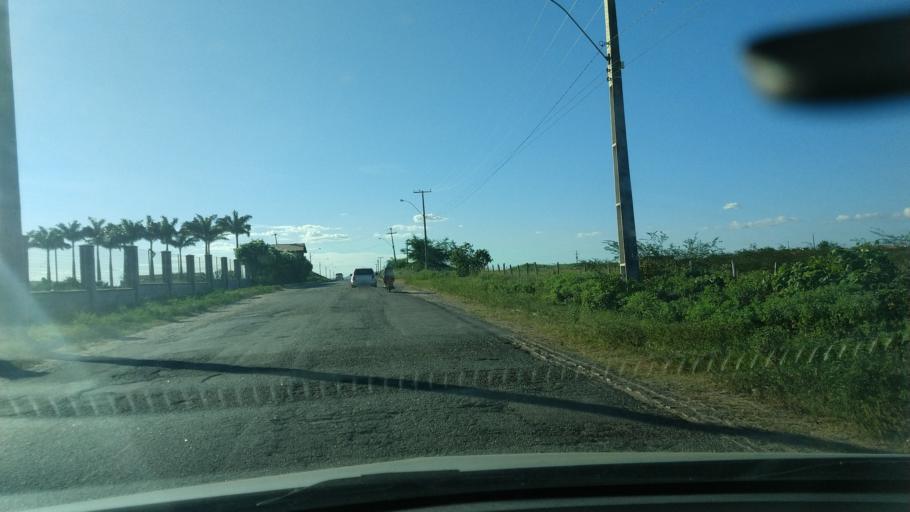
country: BR
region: Rio Grande do Norte
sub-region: Sao Jose Do Campestre
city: Sao Jose do Campestre
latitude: -6.4227
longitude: -35.6479
